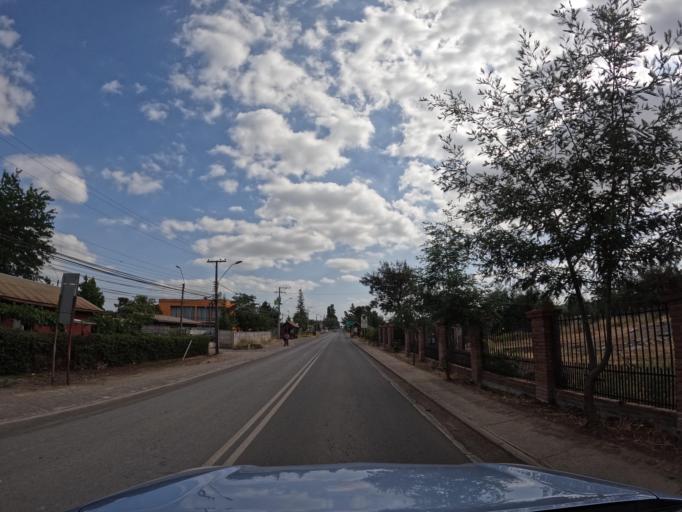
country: CL
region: Maule
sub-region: Provincia de Curico
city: Molina
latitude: -35.1604
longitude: -71.2863
